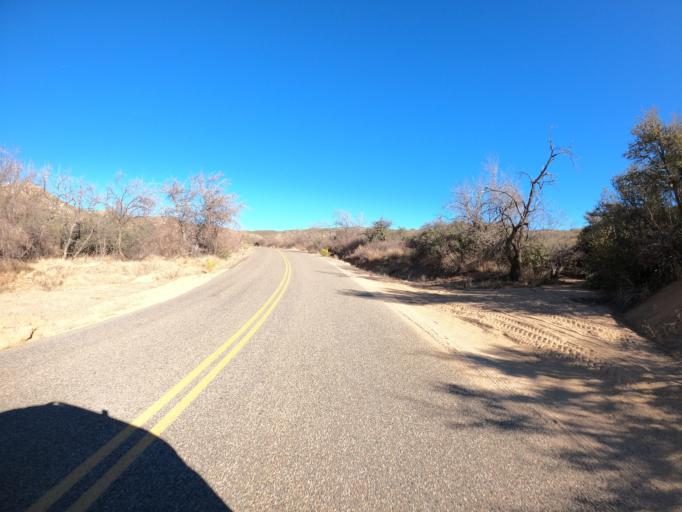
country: US
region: Arizona
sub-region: Yavapai County
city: Dewey-Humboldt
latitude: 34.5510
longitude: -112.0744
